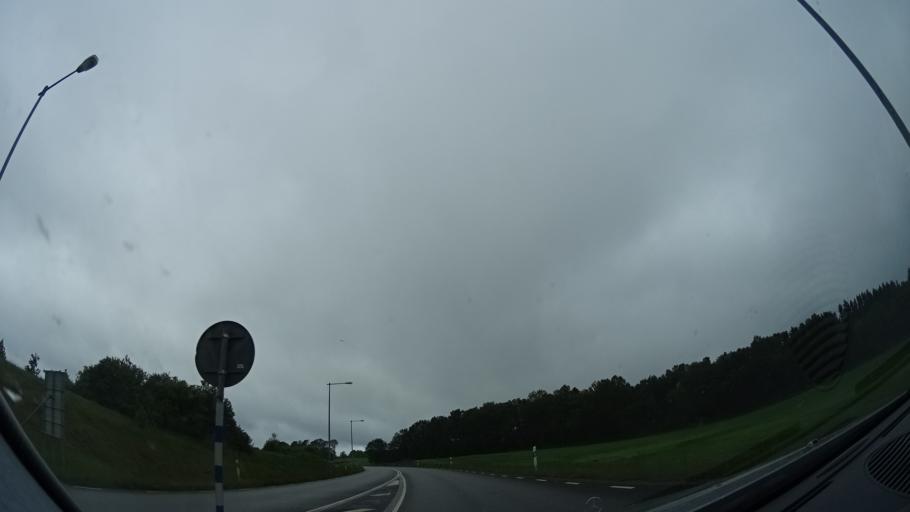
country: SE
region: Skane
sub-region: Hoors Kommun
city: Hoeoer
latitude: 55.9463
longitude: 13.5381
